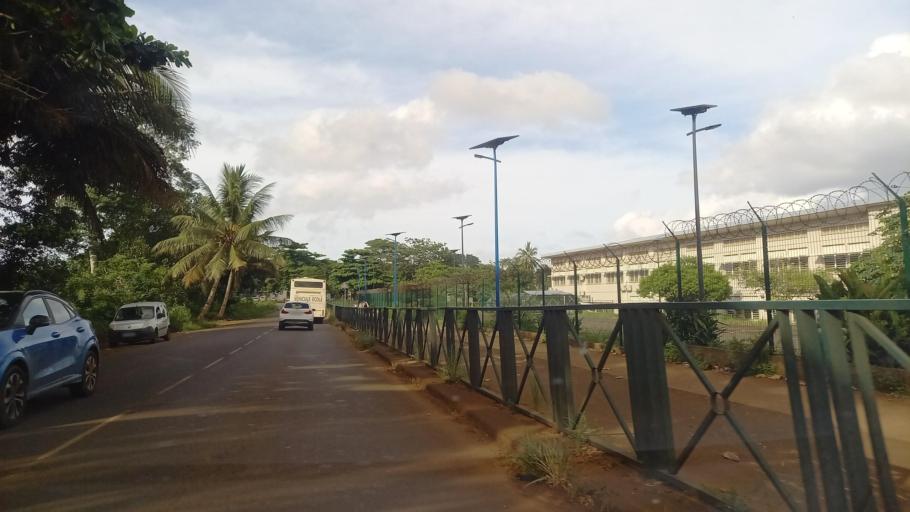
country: YT
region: Tsingoni
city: Tsingoni
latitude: -12.7906
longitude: 45.1267
